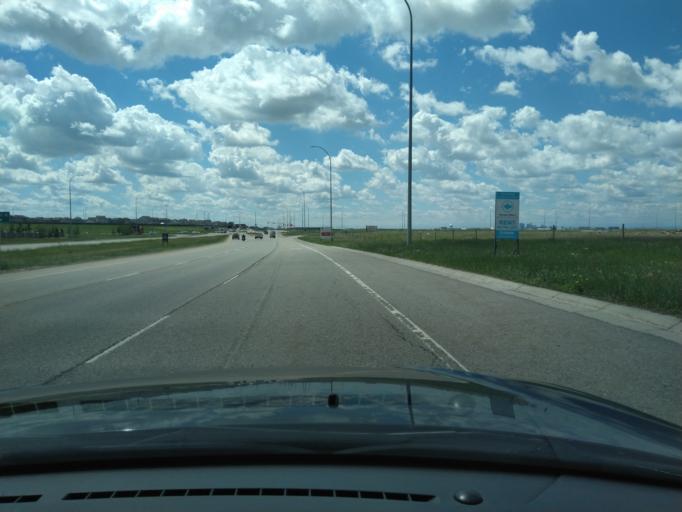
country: CA
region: Alberta
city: Airdrie
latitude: 51.1684
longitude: -113.9703
